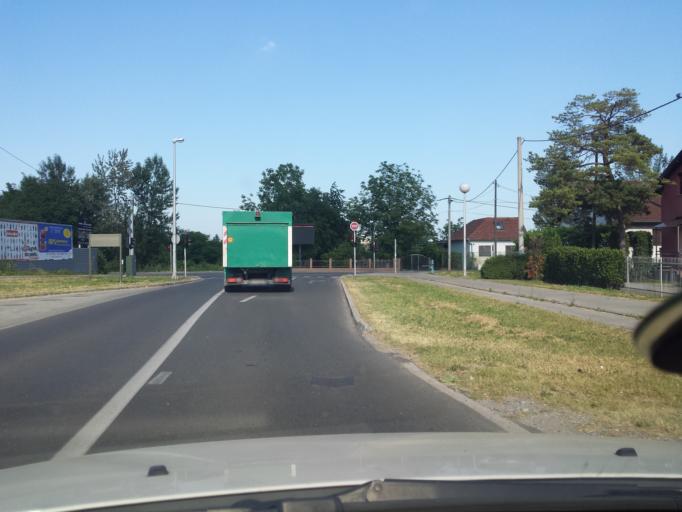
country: HR
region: Grad Zagreb
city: Jankomir
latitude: 45.8064
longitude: 15.9074
